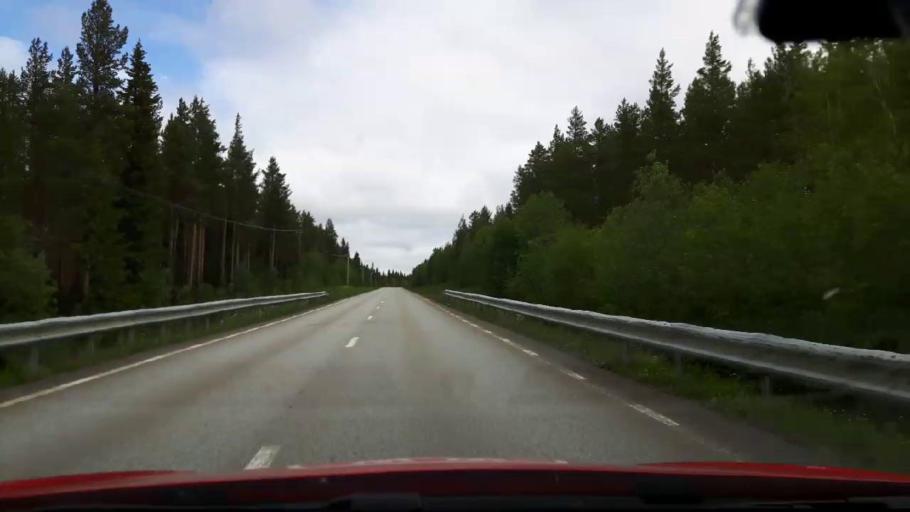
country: SE
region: Jaemtland
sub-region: Krokoms Kommun
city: Krokom
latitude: 63.4633
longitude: 14.4936
